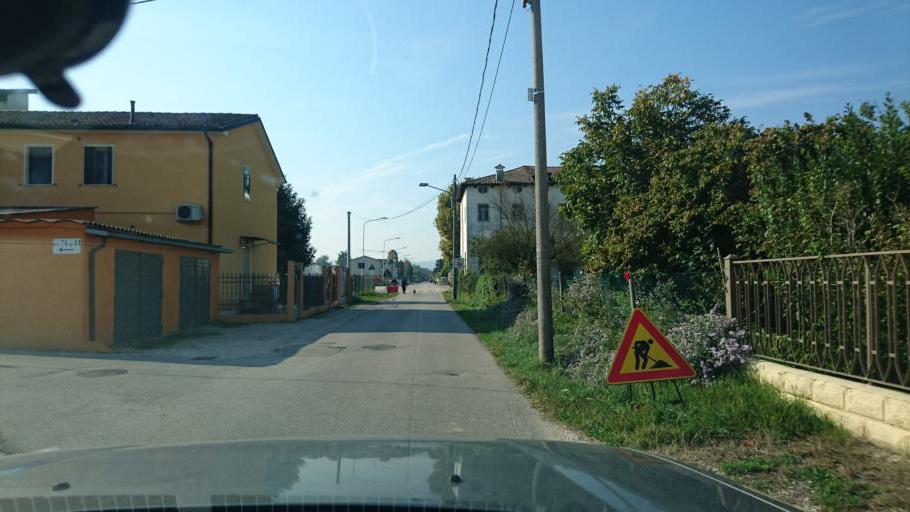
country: IT
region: Veneto
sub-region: Provincia di Vicenza
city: Villaggio Montegrappa
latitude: 45.5366
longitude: 11.5816
